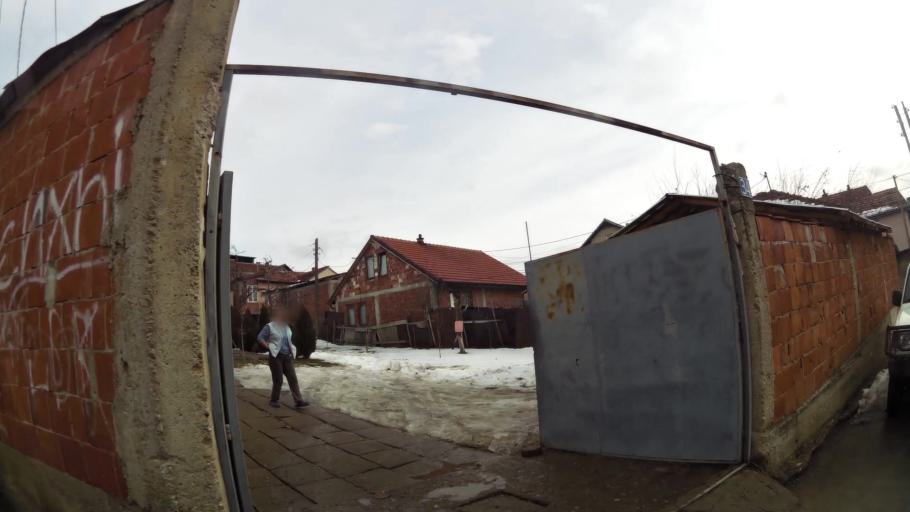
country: XK
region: Pristina
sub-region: Komuna e Prishtines
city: Pristina
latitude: 42.6822
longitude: 21.1659
